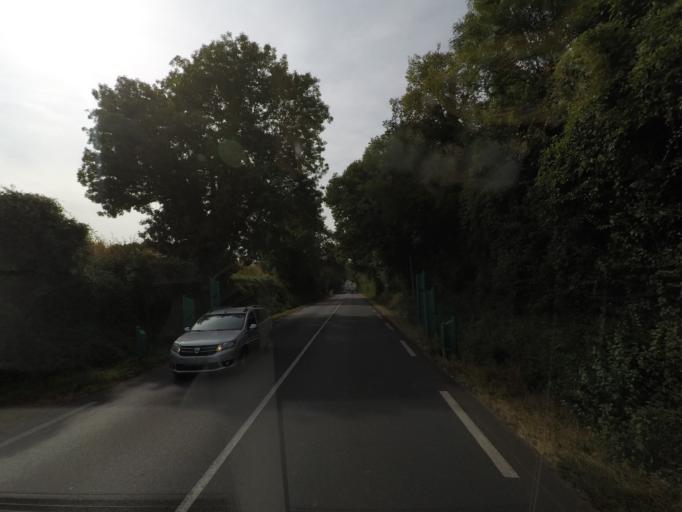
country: FR
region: Poitou-Charentes
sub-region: Departement des Deux-Sevres
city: Melle
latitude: 46.2177
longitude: -0.1261
